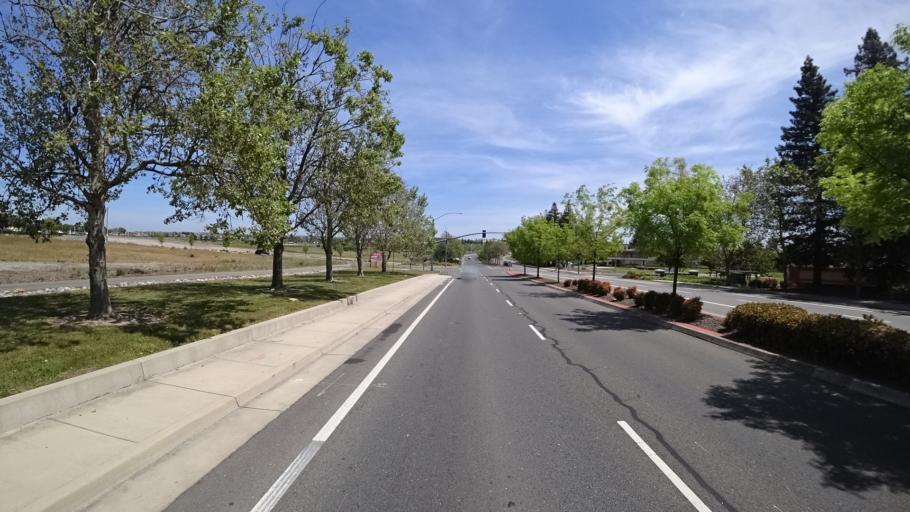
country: US
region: California
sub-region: Placer County
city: Rocklin
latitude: 38.8173
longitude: -121.2933
